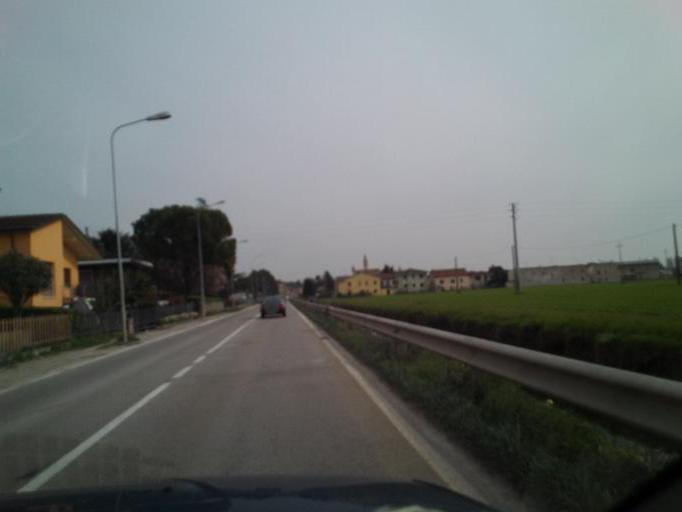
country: IT
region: Lombardy
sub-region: Provincia di Mantova
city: Roverbella
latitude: 45.2638
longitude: 10.7621
